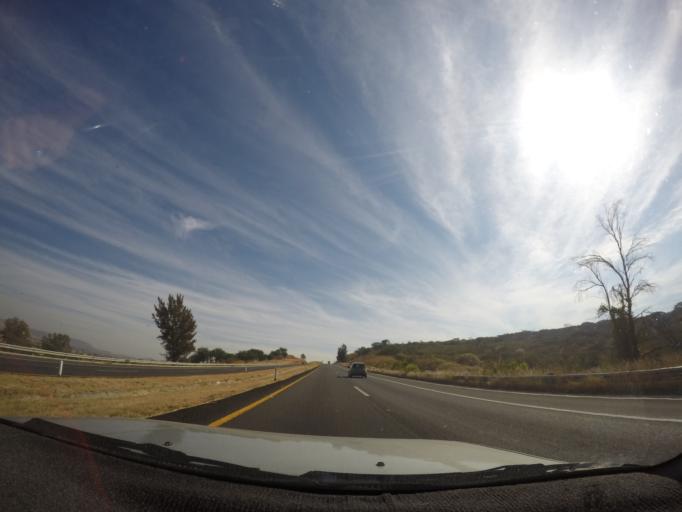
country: MX
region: Puebla
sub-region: Xicotepec
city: San Lorenzo
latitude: 20.4348
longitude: -97.9036
